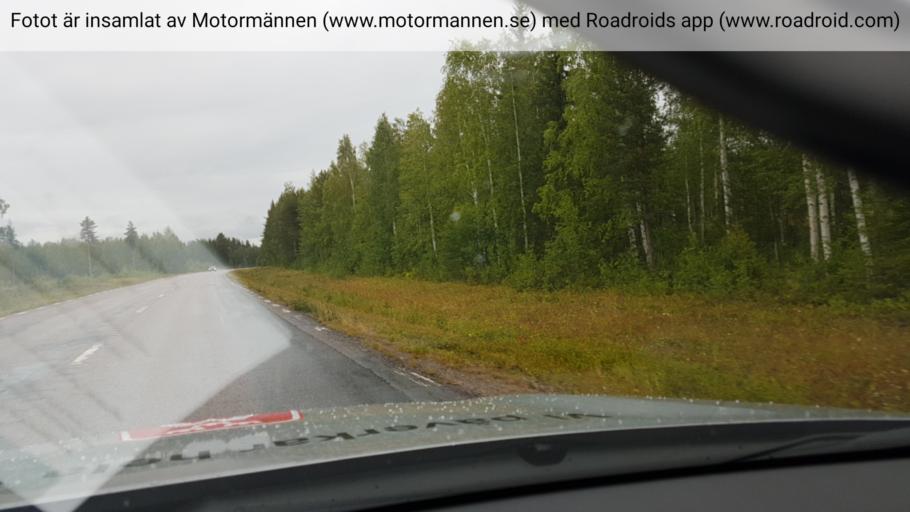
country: SE
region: Norrbotten
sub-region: Alvsbyns Kommun
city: AElvsbyn
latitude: 66.2064
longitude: 20.8786
